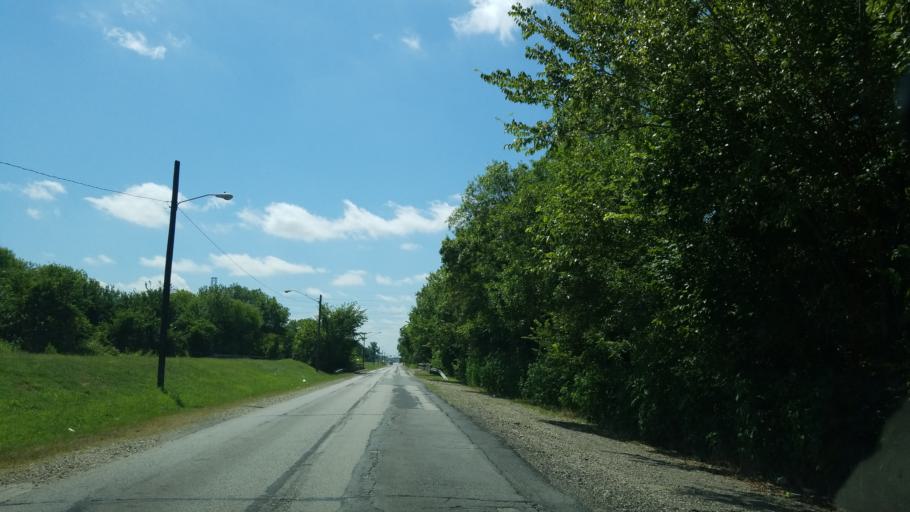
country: US
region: Texas
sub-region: Dallas County
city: Dallas
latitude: 32.7517
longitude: -96.7337
